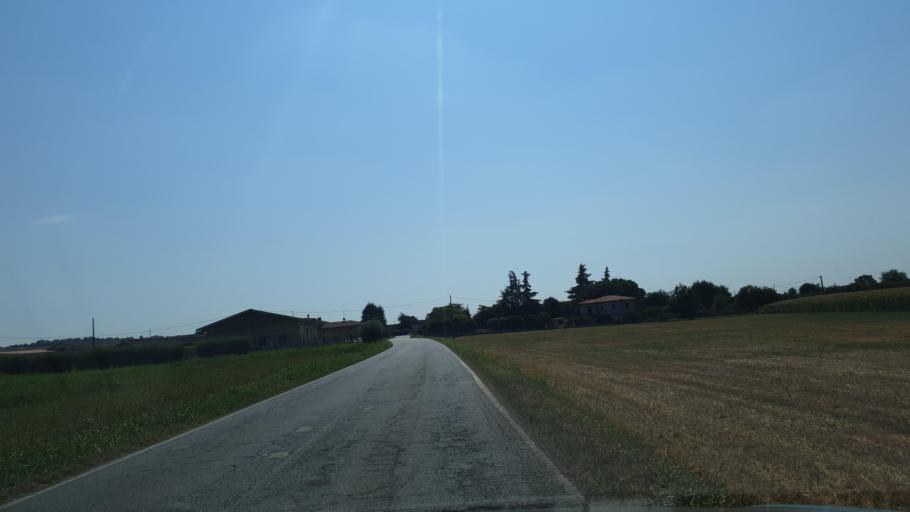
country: IT
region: Lombardy
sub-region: Provincia di Brescia
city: Lonato
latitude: 45.4910
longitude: 10.4683
